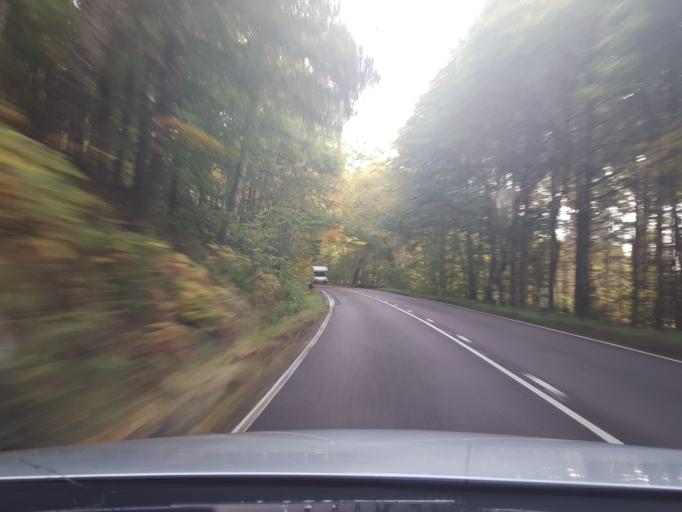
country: GB
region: Scotland
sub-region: Highland
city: Beauly
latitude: 57.2122
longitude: -4.6057
